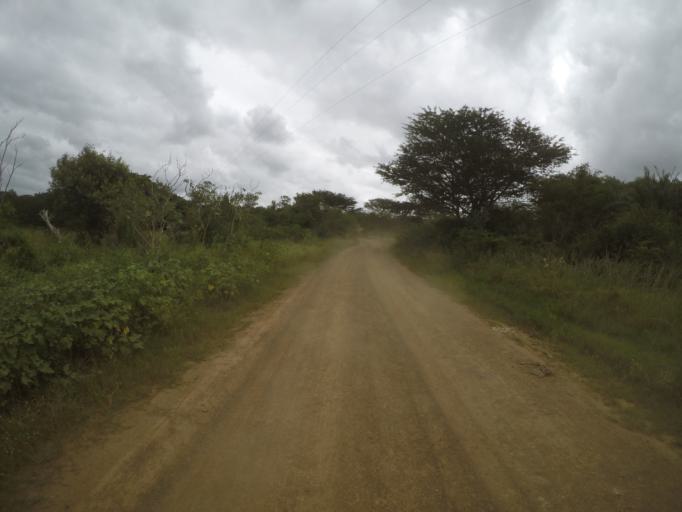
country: ZA
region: KwaZulu-Natal
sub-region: uThungulu District Municipality
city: Empangeni
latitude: -28.5642
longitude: 31.8676
